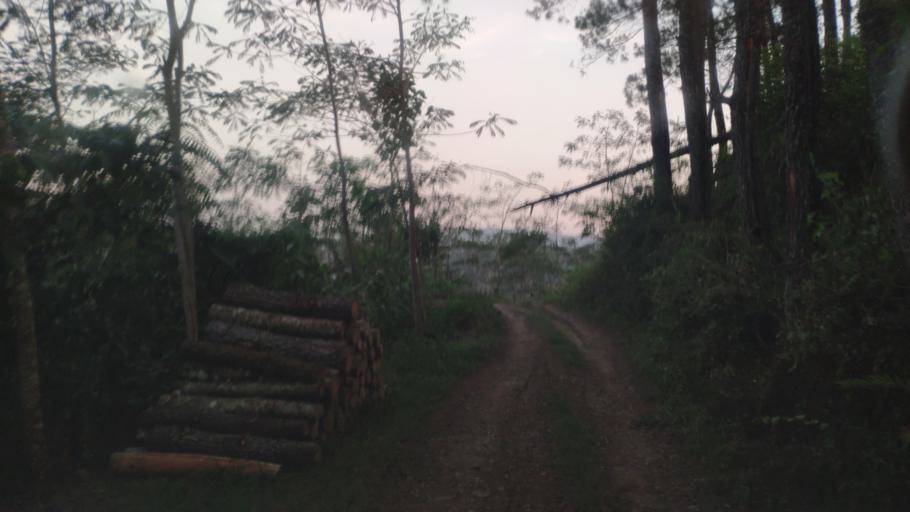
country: ID
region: Central Java
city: Buaran
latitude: -7.2663
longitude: 109.5805
